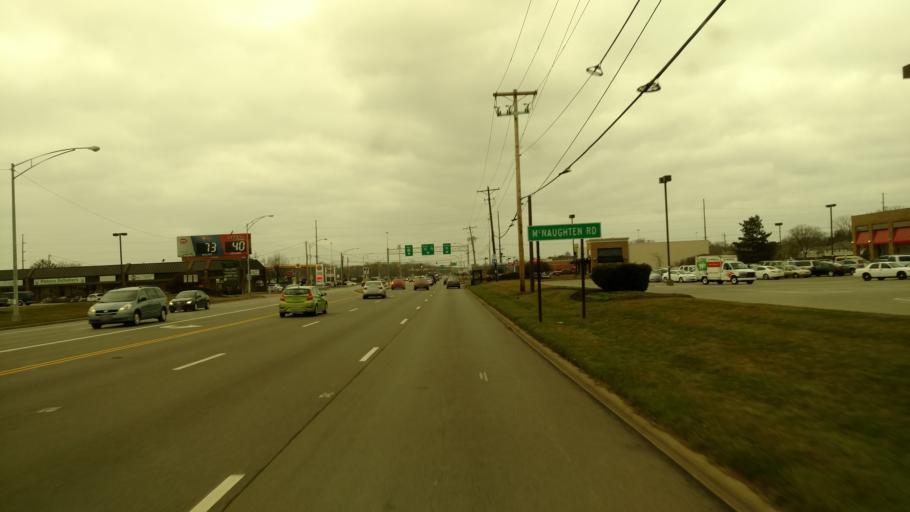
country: US
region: Ohio
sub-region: Franklin County
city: Reynoldsburg
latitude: 39.9549
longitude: -82.8359
